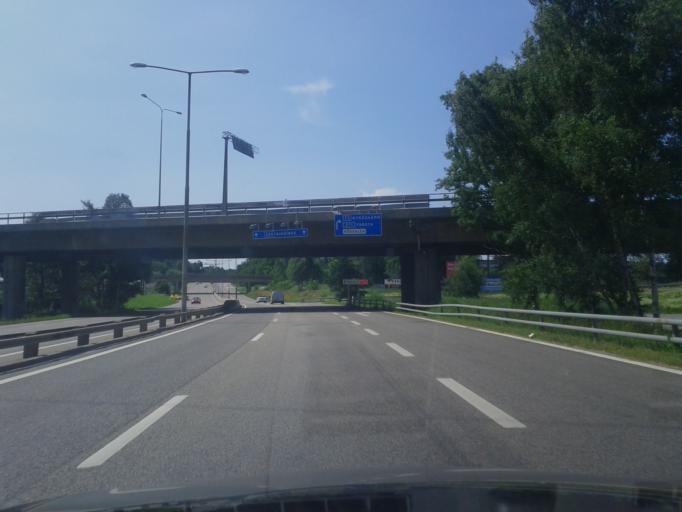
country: SE
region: Stockholm
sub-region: Stockholms Kommun
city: Arsta
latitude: 59.2740
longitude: 18.0130
